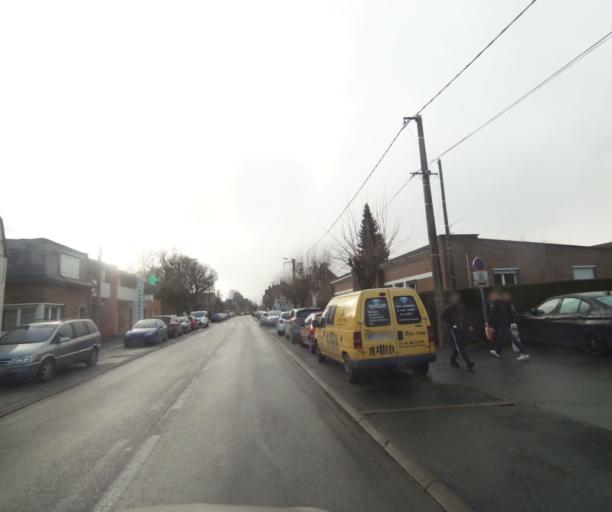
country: FR
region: Nord-Pas-de-Calais
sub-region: Departement du Nord
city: Famars
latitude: 50.3190
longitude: 3.5184
